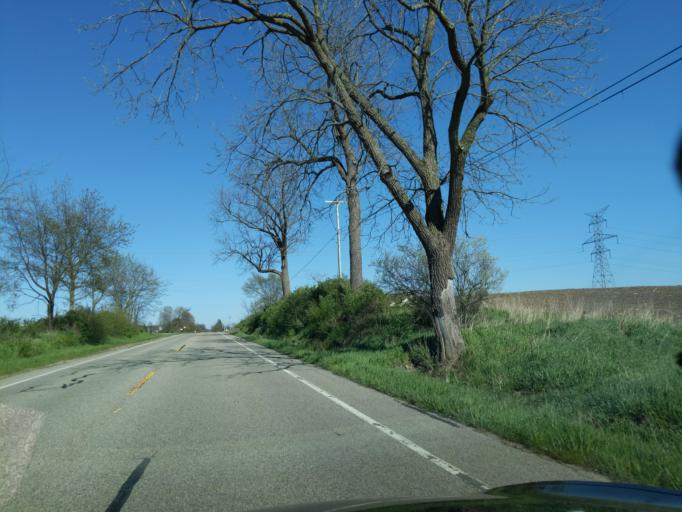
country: US
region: Michigan
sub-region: Kent County
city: Lowell
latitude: 42.8853
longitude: -85.4265
